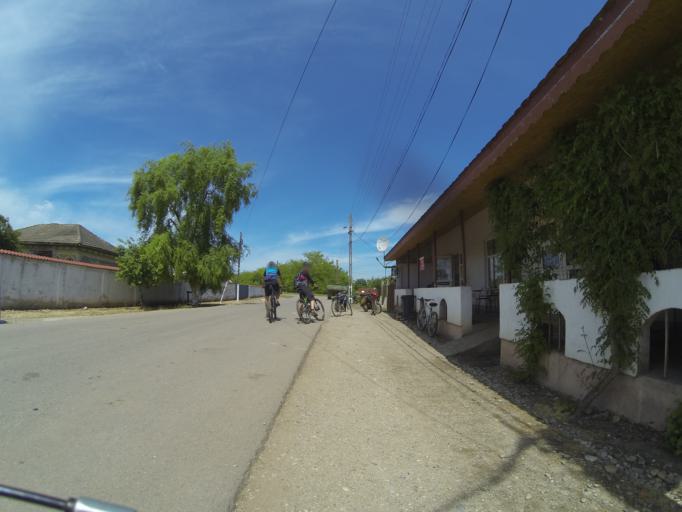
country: RO
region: Dolj
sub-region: Comuna Diosti
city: Radomir
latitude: 44.1599
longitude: 24.1626
